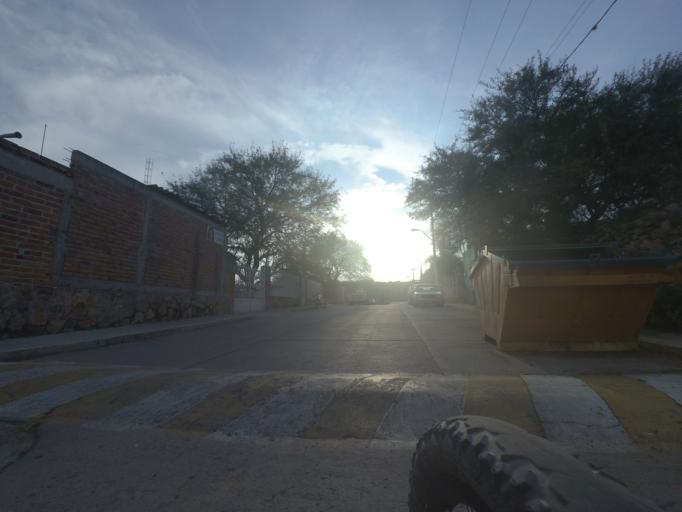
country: MX
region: Aguascalientes
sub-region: Aguascalientes
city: Los Canos
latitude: 21.7804
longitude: -102.3762
